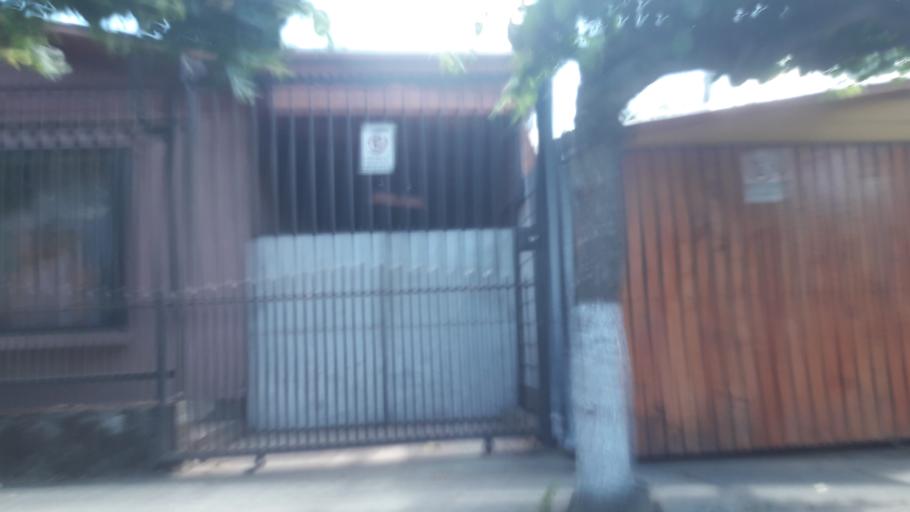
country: CL
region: Biobio
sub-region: Provincia de Biobio
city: Nacimiento
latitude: -37.5053
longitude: -72.6845
